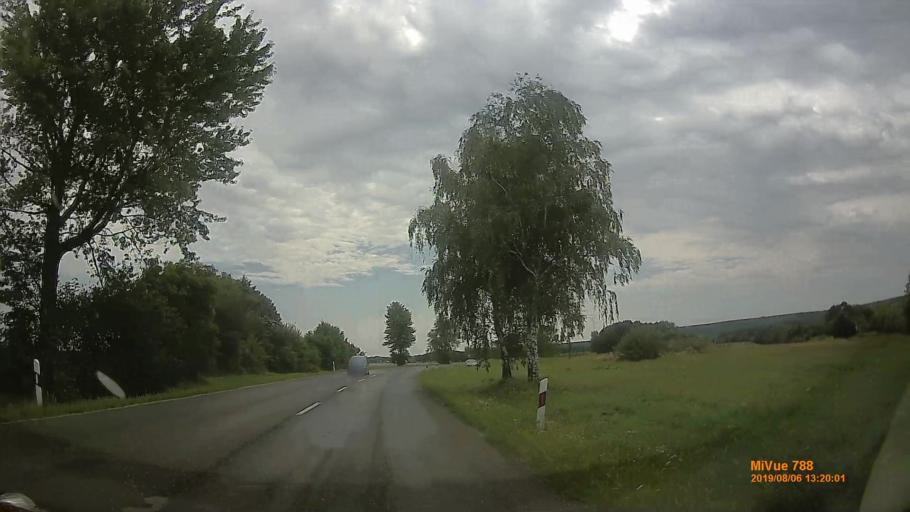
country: HU
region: Vas
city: Koszeg
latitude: 47.3589
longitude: 16.5681
